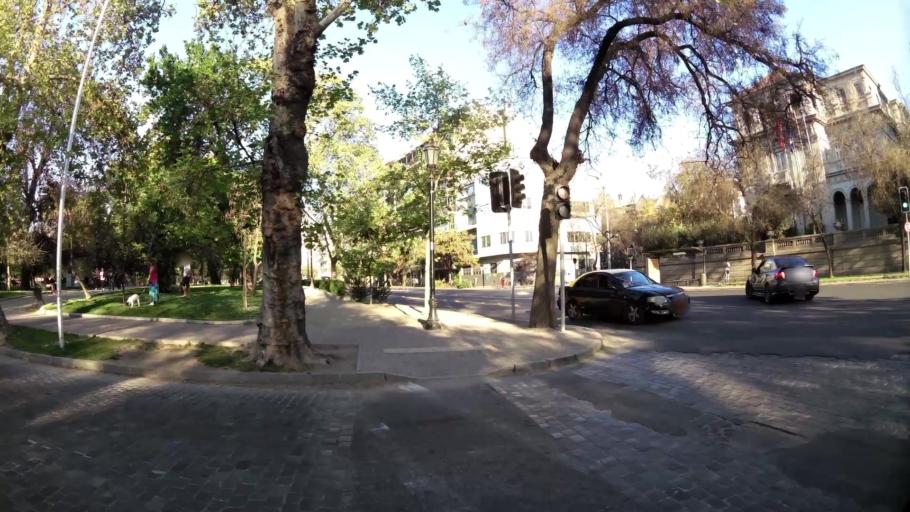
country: CL
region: Santiago Metropolitan
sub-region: Provincia de Santiago
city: Santiago
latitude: -33.4368
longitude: -70.6393
